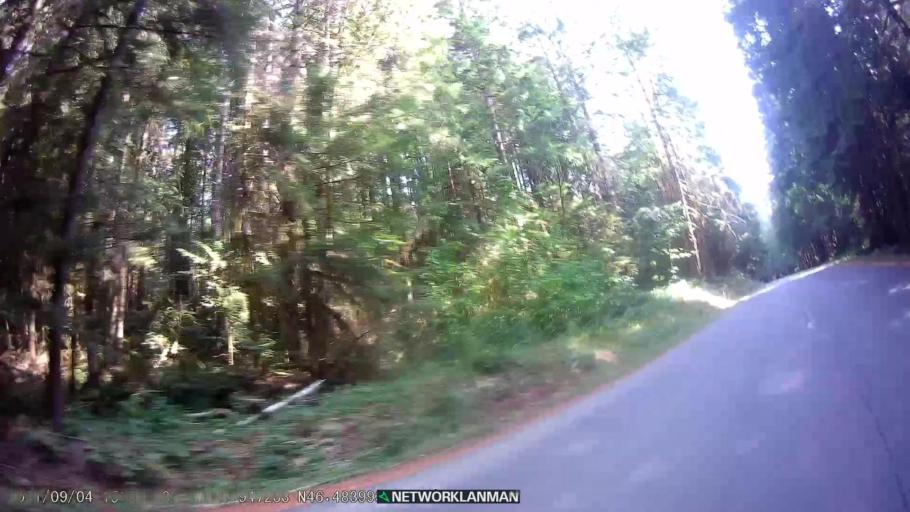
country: US
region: Washington
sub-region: Lewis County
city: Morton
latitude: 46.4839
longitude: -121.9474
